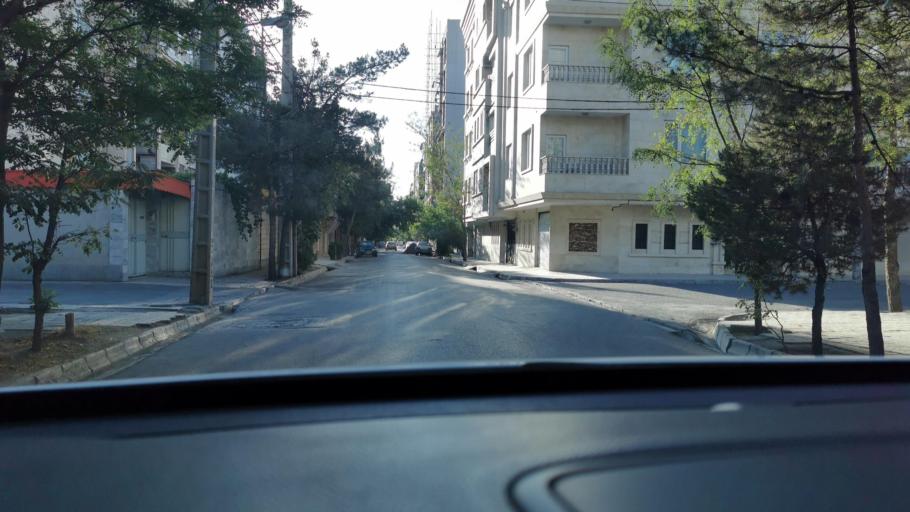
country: IR
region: Razavi Khorasan
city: Mashhad
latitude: 36.3616
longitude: 59.4875
